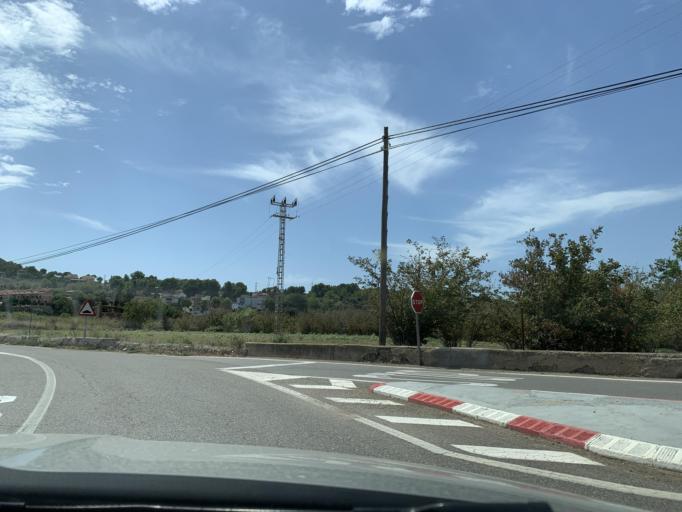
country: ES
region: Catalonia
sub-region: Provincia de Tarragona
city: Altafulla
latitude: 41.1610
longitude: 1.3633
